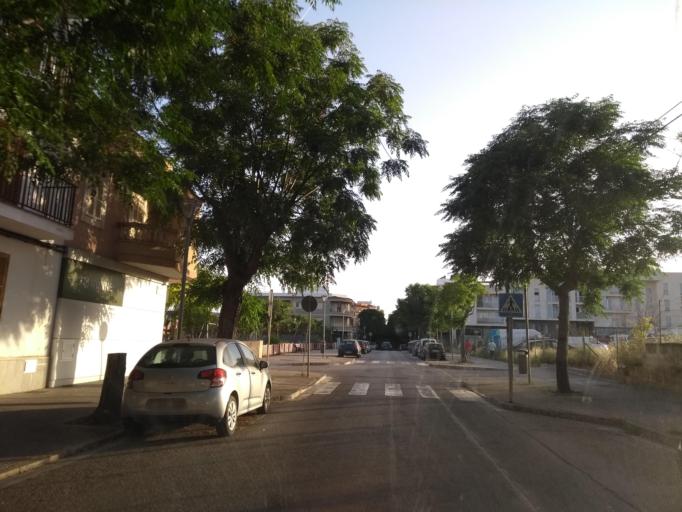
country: ES
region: Balearic Islands
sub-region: Illes Balears
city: Inca
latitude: 39.7247
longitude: 2.9185
